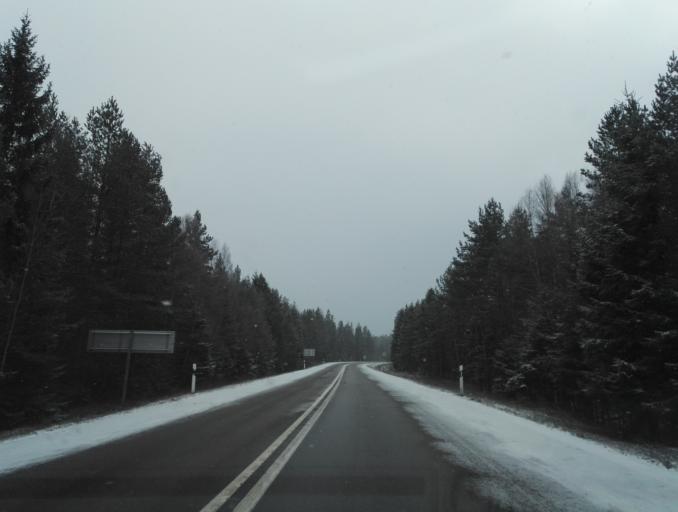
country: SE
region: Kronoberg
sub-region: Uppvidinge Kommun
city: Lenhovda
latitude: 56.9170
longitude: 15.3645
